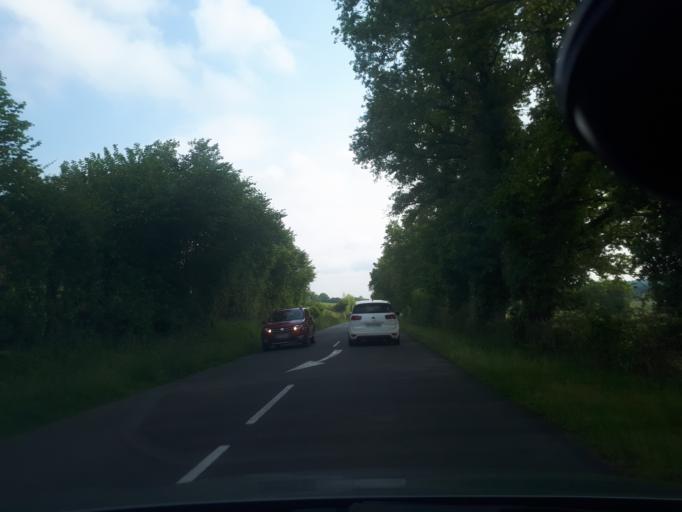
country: FR
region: Auvergne
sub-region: Departement de l'Allier
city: Dompierre-sur-Besbre
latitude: 46.4168
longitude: 3.6112
